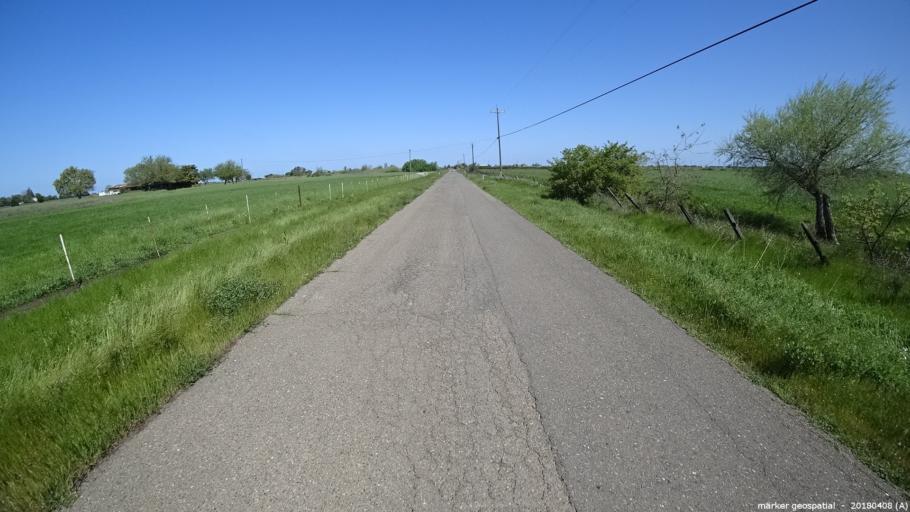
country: US
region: California
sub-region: San Joaquin County
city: Thornton
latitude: 38.2851
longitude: -121.4198
